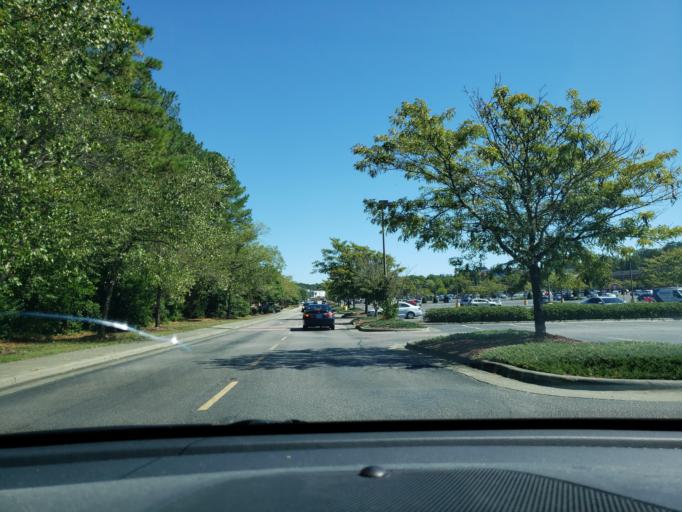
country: US
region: North Carolina
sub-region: Durham County
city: Durham
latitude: 35.9676
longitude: -78.9600
